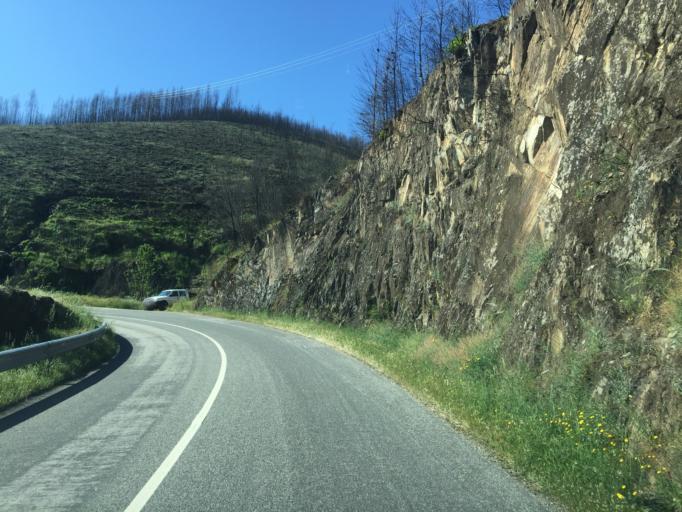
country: PT
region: Coimbra
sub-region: Pampilhosa da Serra
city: Pampilhosa da Serra
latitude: 40.0404
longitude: -7.9420
